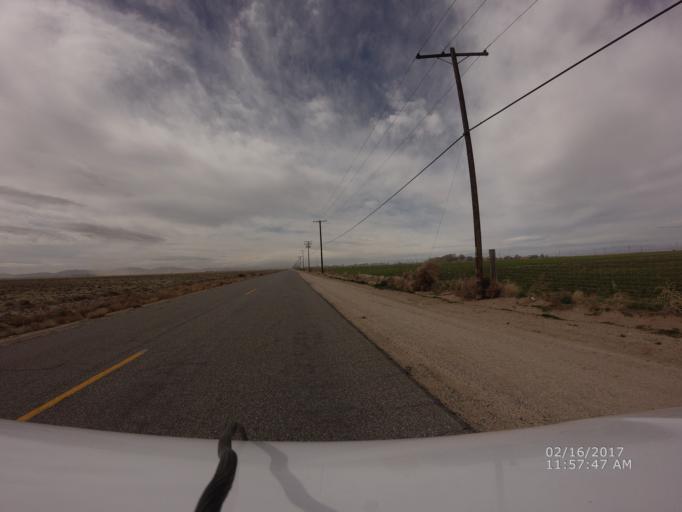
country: US
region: California
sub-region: Los Angeles County
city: Lake Los Angeles
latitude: 34.6900
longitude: -117.9183
